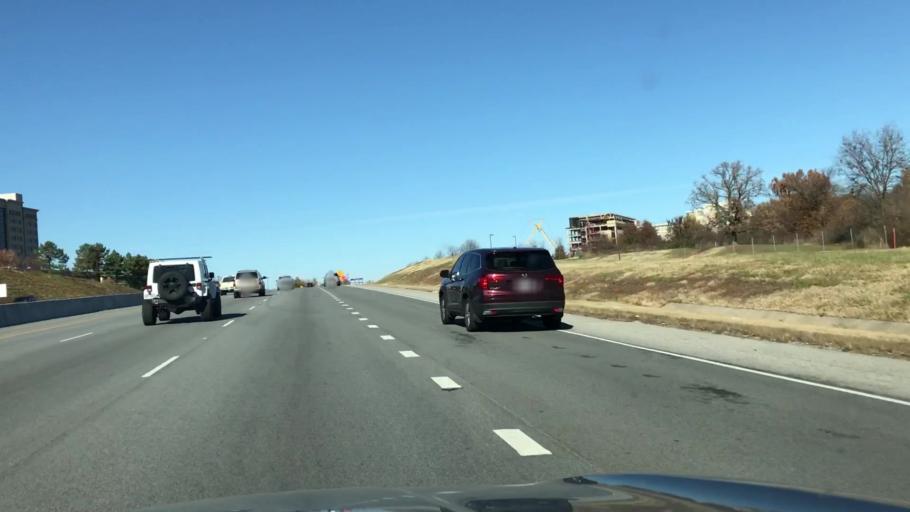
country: US
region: Arkansas
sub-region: Benton County
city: Cave Springs
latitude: 36.3040
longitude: -94.1824
